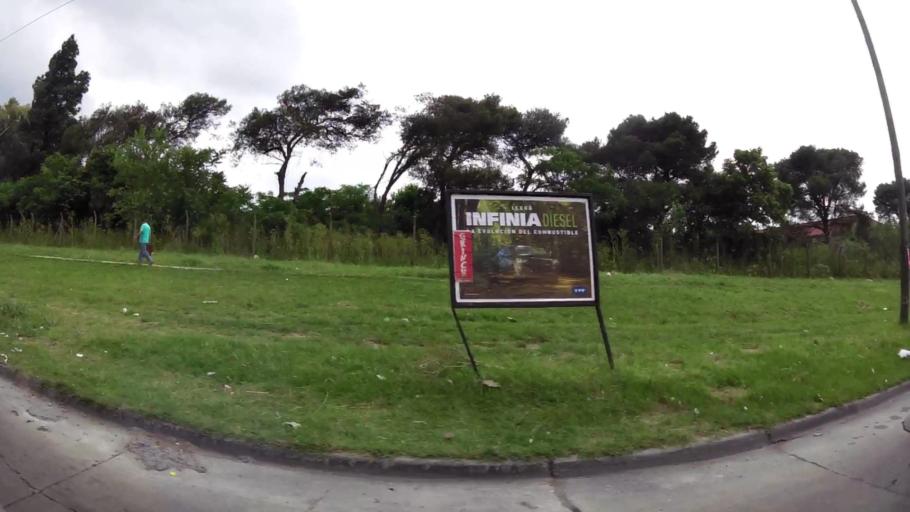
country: AR
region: Buenos Aires
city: San Justo
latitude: -34.6977
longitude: -58.5373
